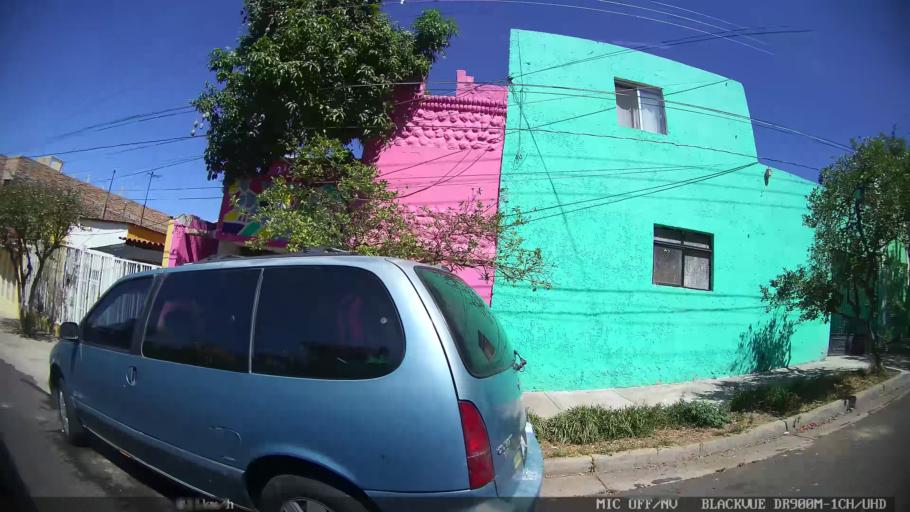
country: MX
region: Jalisco
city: Tlaquepaque
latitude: 20.6915
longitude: -103.2811
